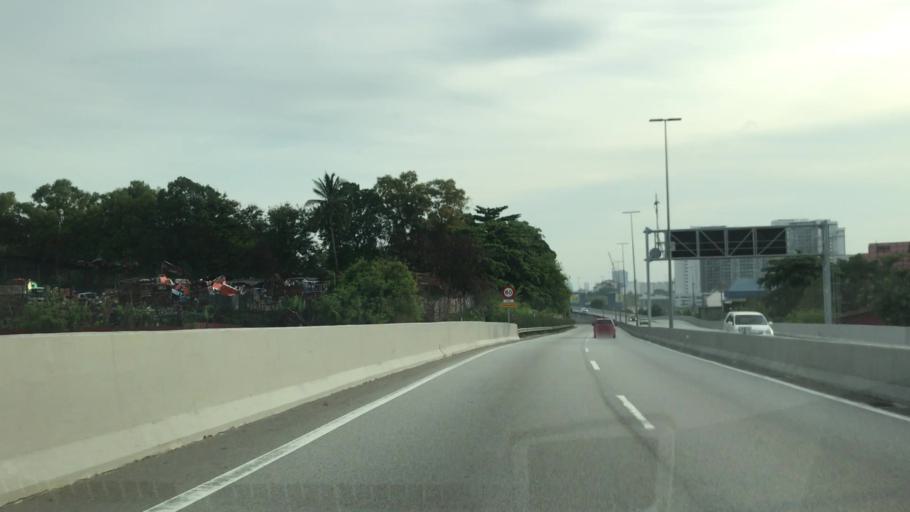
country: MY
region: Kuala Lumpur
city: Kuala Lumpur
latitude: 3.1105
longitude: 101.7103
